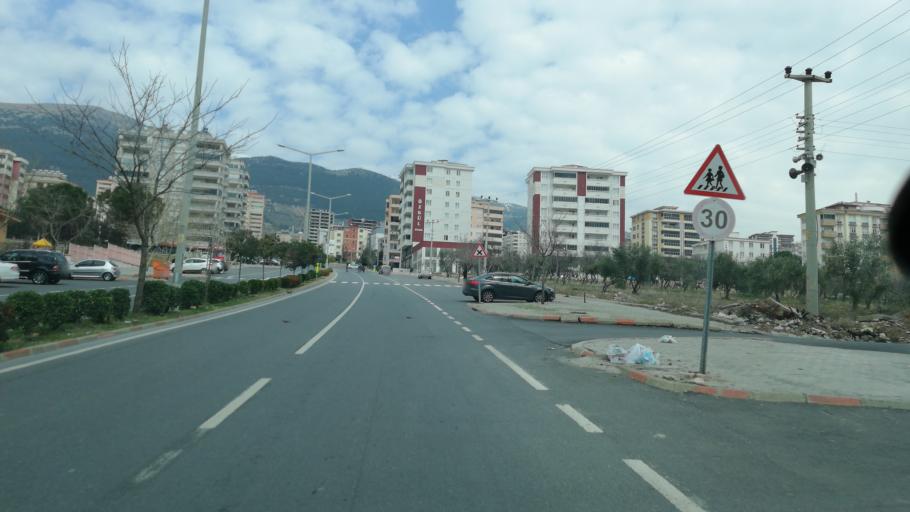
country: TR
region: Kahramanmaras
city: Kahramanmaras
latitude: 37.5877
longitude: 36.8622
